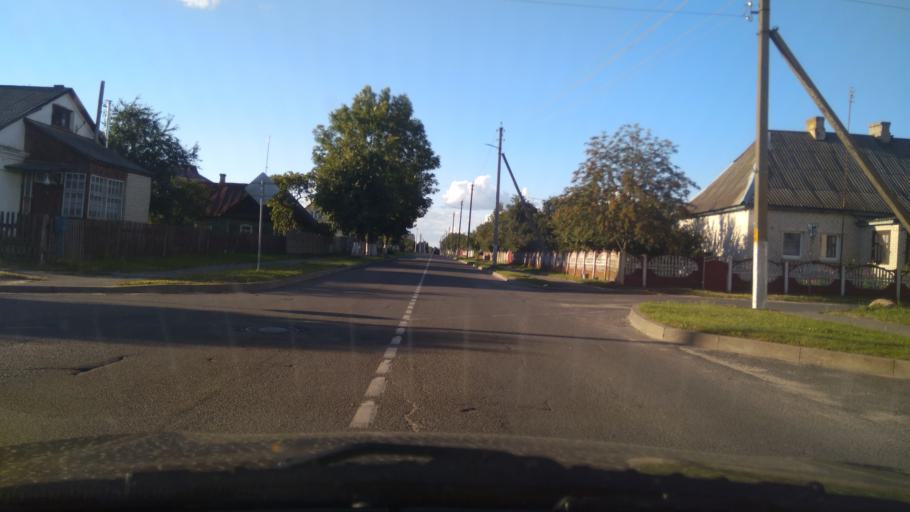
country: BY
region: Brest
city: Pruzhany
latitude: 52.5625
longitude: 24.4629
